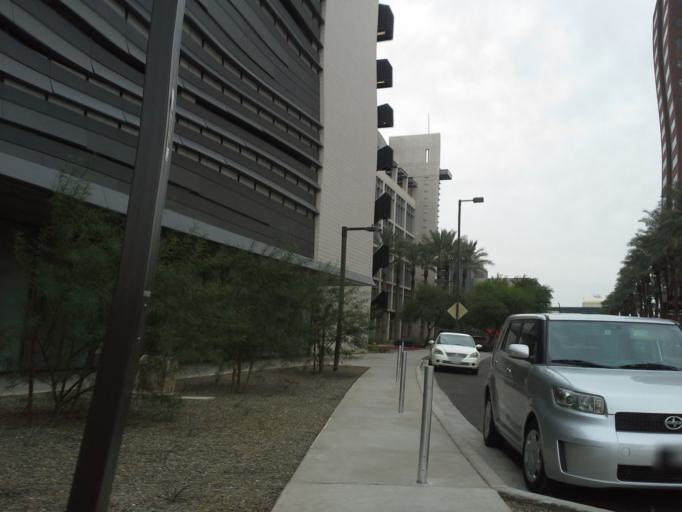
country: US
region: Arizona
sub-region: Maricopa County
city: Phoenix
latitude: 33.4540
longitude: -112.0675
